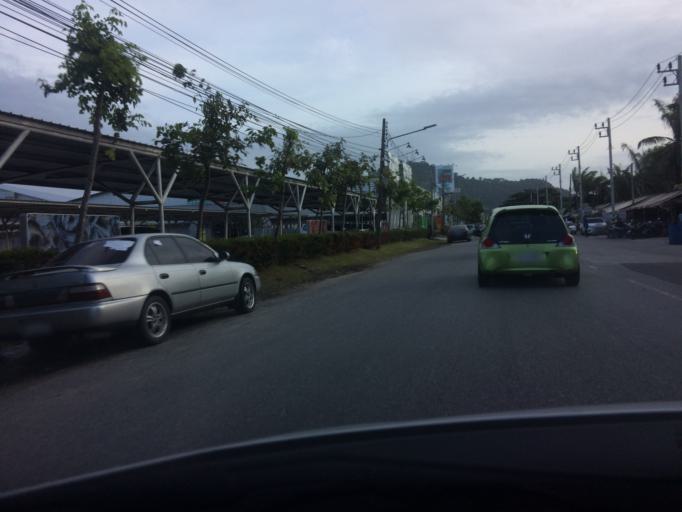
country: TH
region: Phuket
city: Ban Talat Yai
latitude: 7.8768
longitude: 98.3986
